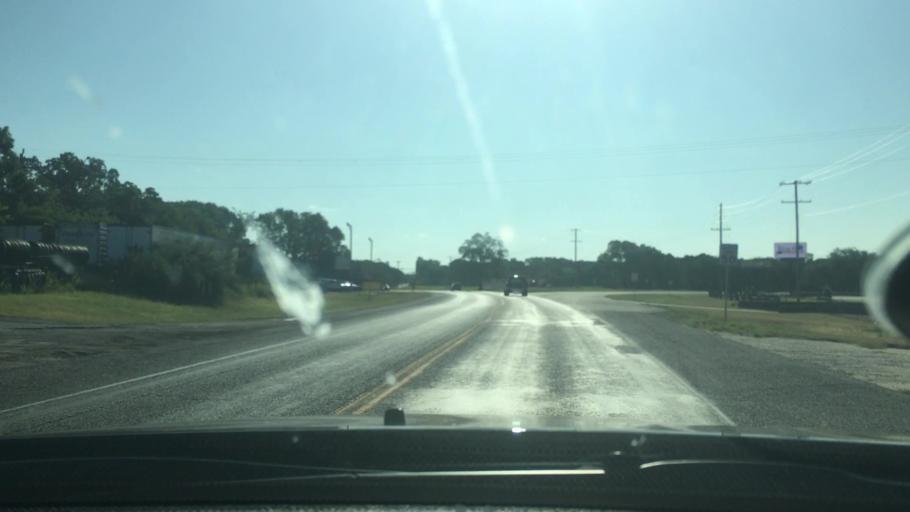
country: US
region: Oklahoma
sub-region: Johnston County
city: Tishomingo
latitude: 34.2371
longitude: -96.7011
